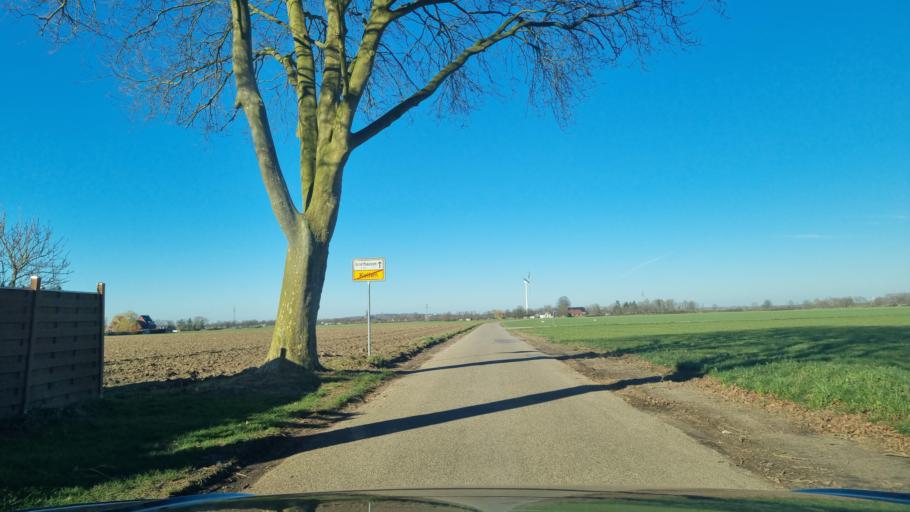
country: DE
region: North Rhine-Westphalia
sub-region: Regierungsbezirk Dusseldorf
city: Kleve
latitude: 51.8047
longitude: 6.1679
